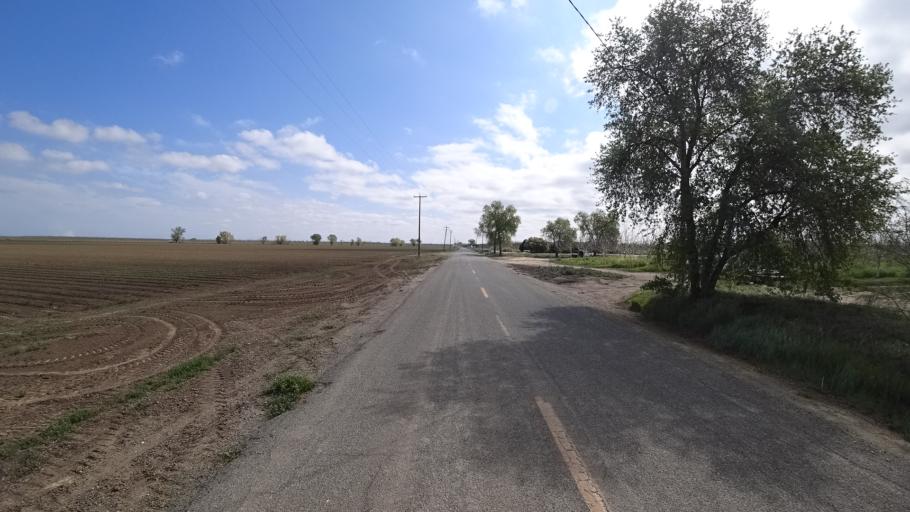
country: US
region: California
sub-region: Colusa County
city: Colusa
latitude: 39.4201
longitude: -121.9547
